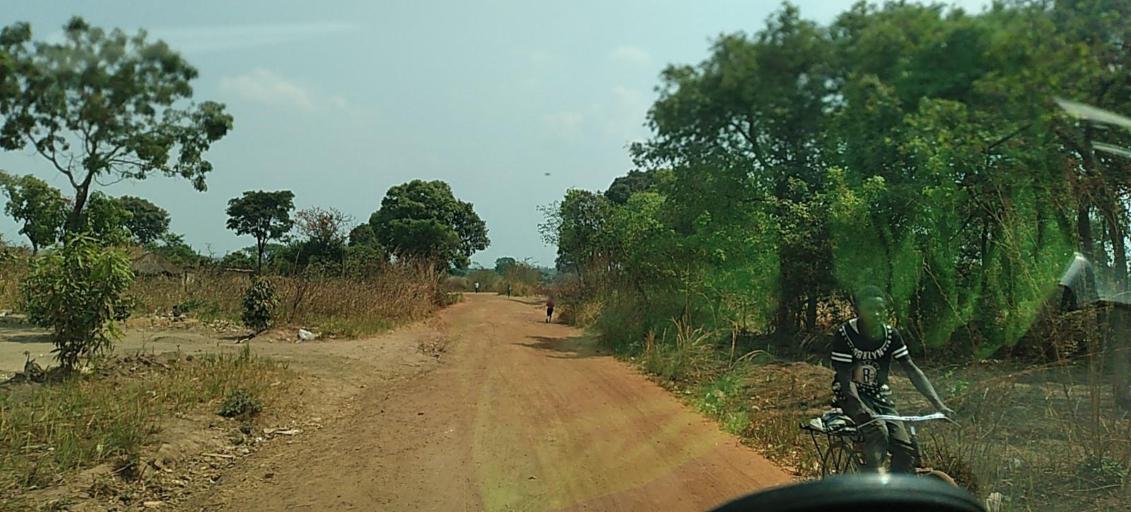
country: ZM
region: North-Western
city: Kansanshi
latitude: -12.0926
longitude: 26.3651
